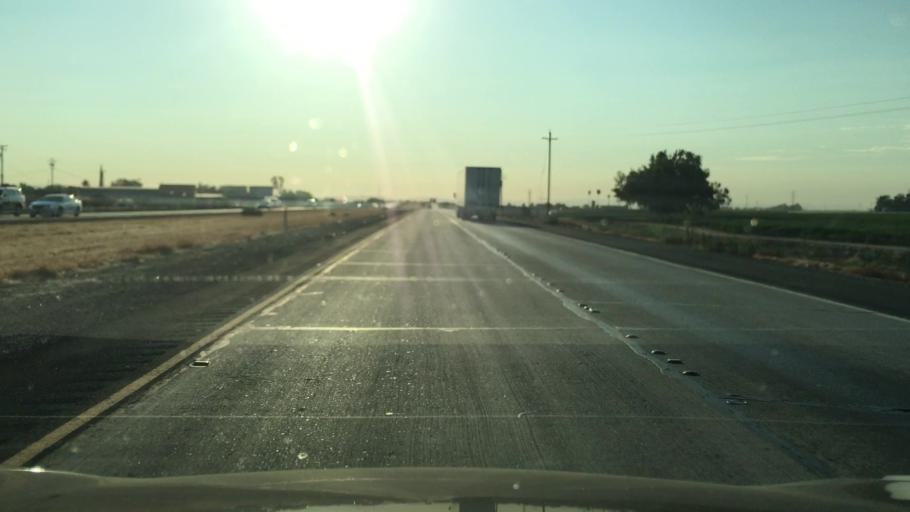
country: US
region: California
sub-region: Merced County
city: Dos Palos
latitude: 37.0485
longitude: -120.6251
